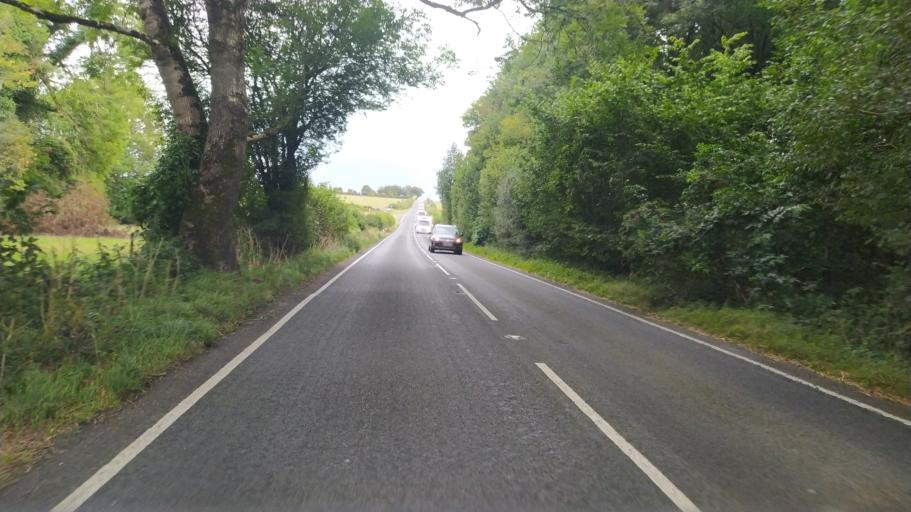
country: GB
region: England
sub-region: Dorset
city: Blandford Forum
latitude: 50.9126
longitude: -2.0598
